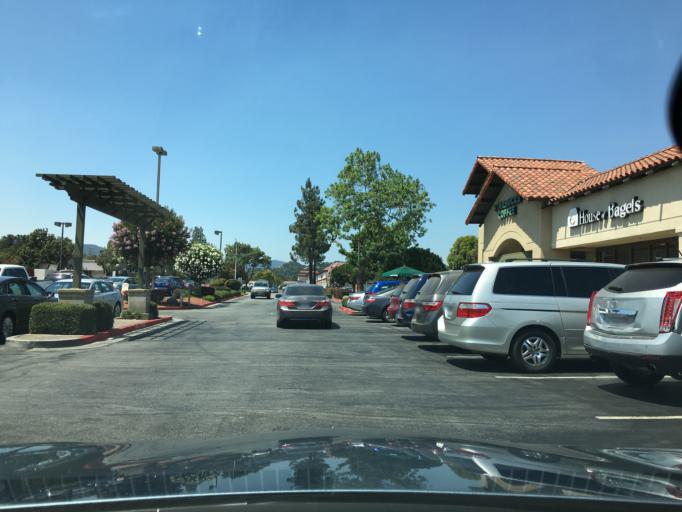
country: US
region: California
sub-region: Santa Clara County
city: Gilroy
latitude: 37.0142
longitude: -121.5856
